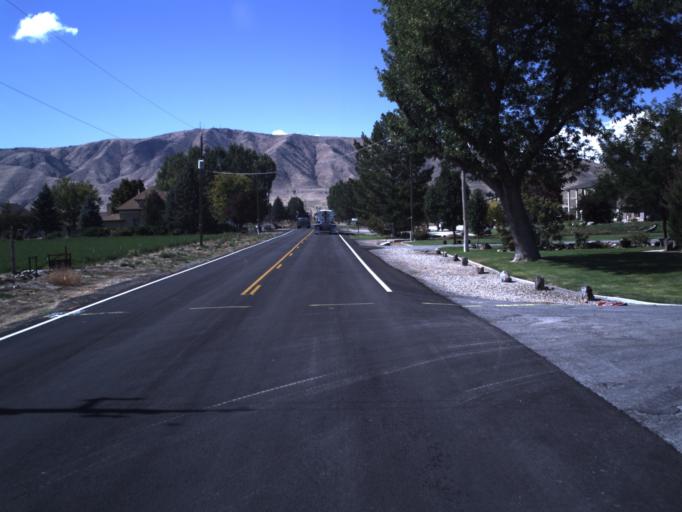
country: US
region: Utah
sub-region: Utah County
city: Benjamin
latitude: 40.0981
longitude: -111.7399
